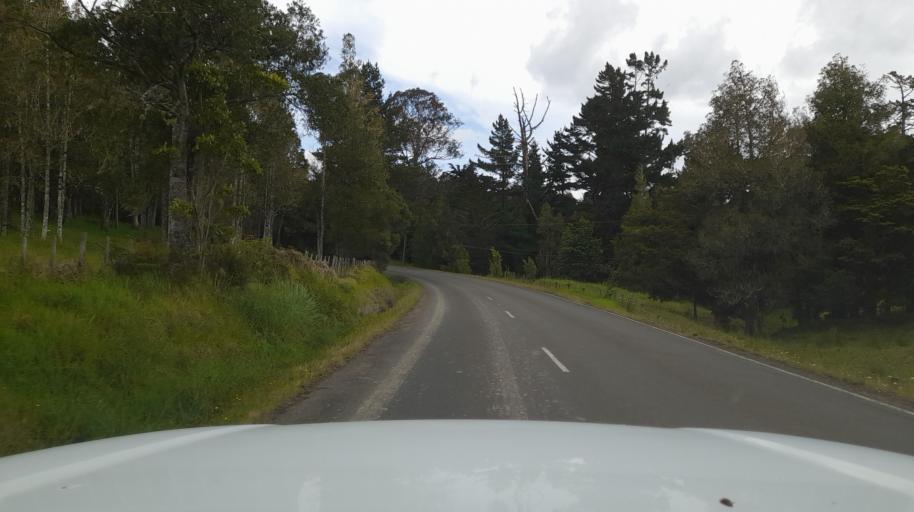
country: NZ
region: Northland
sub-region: Far North District
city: Kaitaia
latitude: -35.3075
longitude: 173.3427
